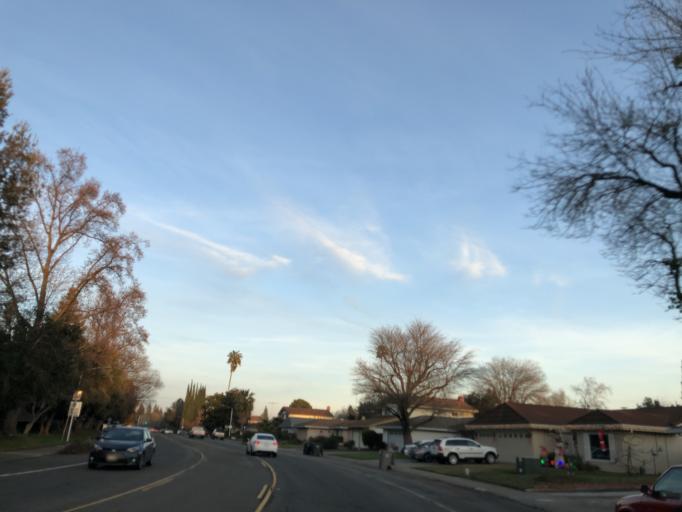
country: US
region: California
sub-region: Sacramento County
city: Rosemont
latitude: 38.5586
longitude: -121.3998
